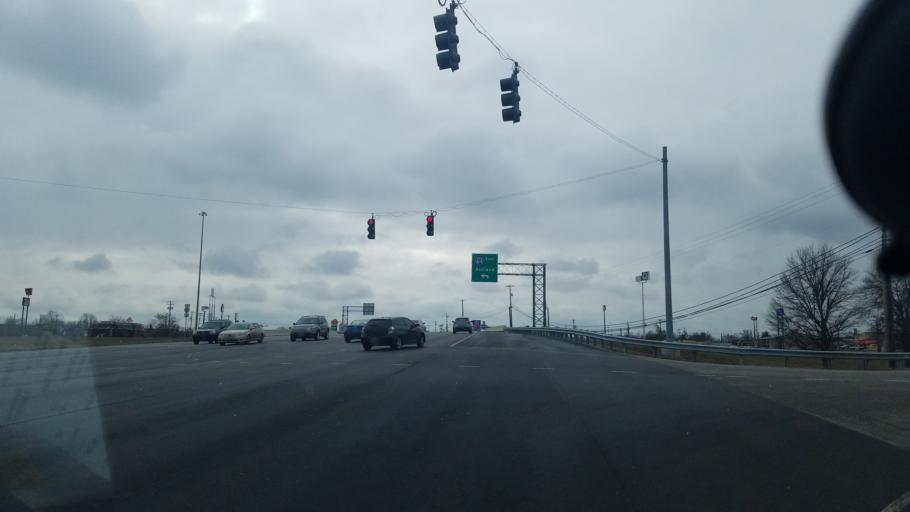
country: US
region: Kentucky
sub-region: Montgomery County
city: Mount Sterling
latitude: 38.0791
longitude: -83.9498
